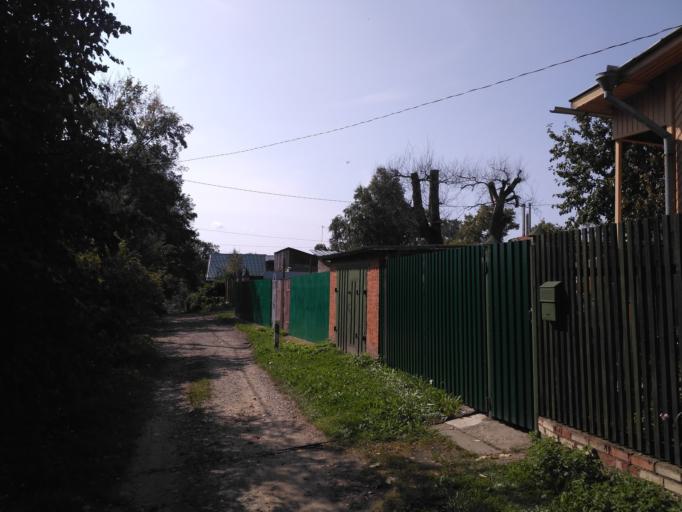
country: RU
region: Moskovskaya
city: Sergiyev Posad
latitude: 56.3059
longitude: 38.1256
